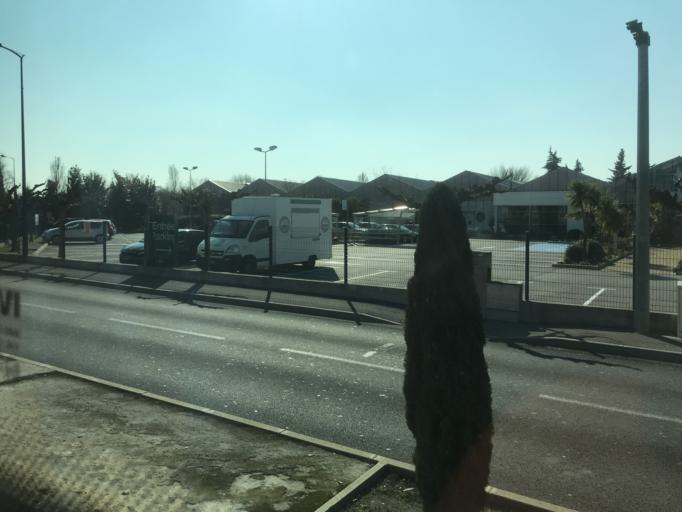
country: FR
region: Languedoc-Roussillon
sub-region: Departement de l'Herault
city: Perols
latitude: 43.5811
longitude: 3.9437
